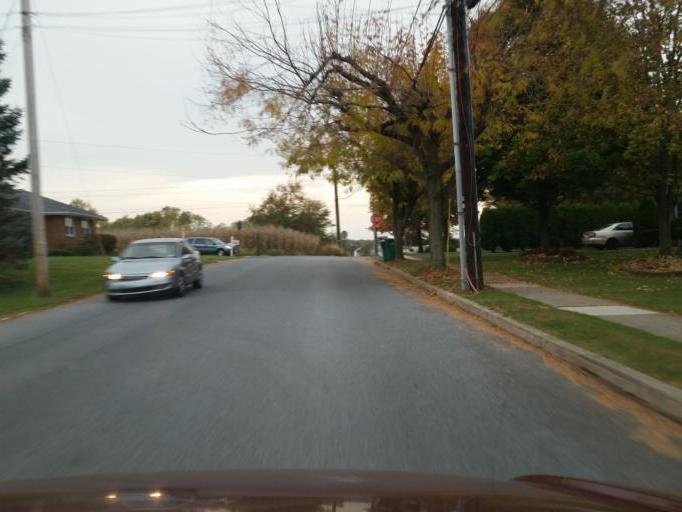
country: US
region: Pennsylvania
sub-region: Dauphin County
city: Hummelstown
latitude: 40.2394
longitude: -76.7146
